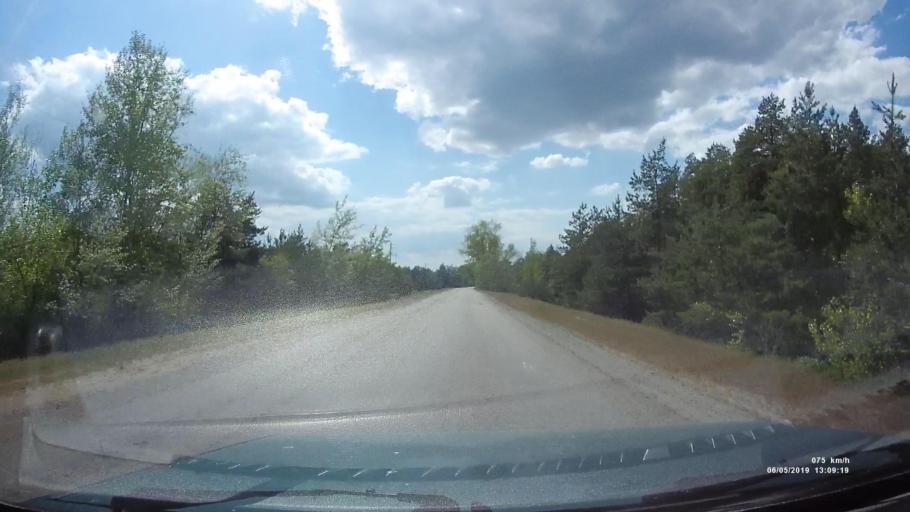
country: RU
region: Rostov
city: Ust'-Donetskiy
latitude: 47.7693
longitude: 40.9855
